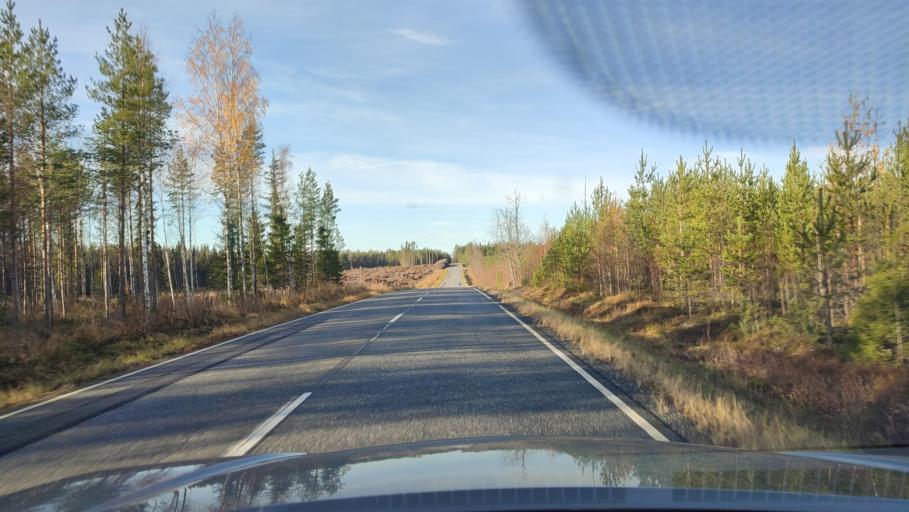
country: FI
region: Ostrobothnia
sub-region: Sydosterbotten
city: Naerpes
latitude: 62.4622
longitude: 21.5290
